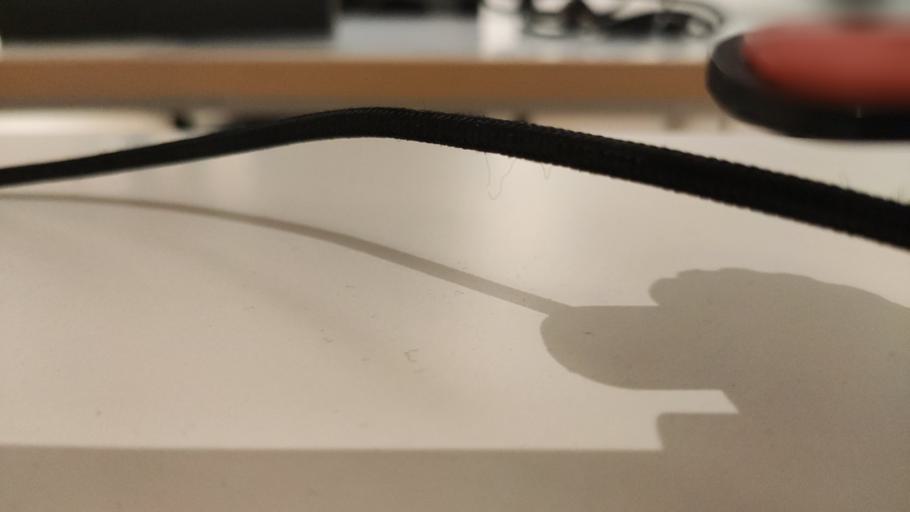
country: RU
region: Kaluga
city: Belousovo
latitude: 55.1436
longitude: 36.7682
